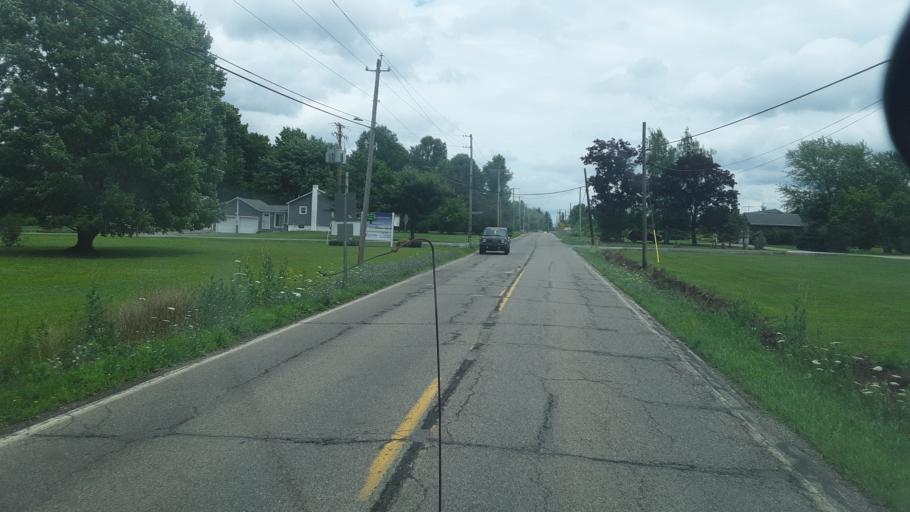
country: US
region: Ohio
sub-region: Trumbull County
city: Churchill
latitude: 41.1841
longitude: -80.6796
